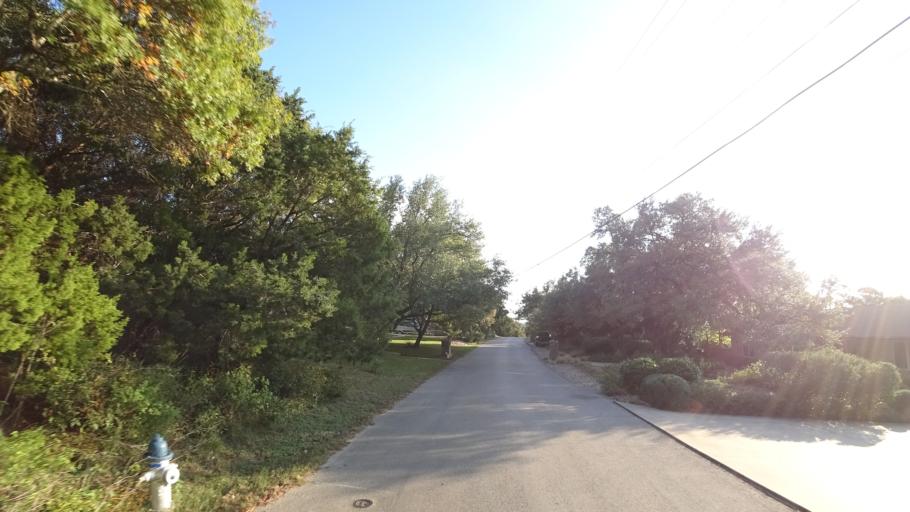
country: US
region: Texas
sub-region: Travis County
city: Lost Creek
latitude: 30.2974
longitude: -97.8407
